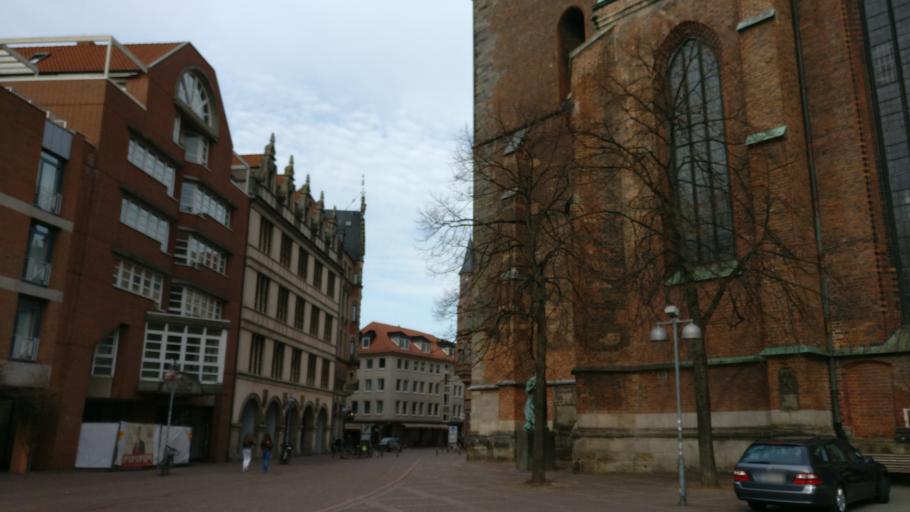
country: DE
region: Lower Saxony
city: Hannover
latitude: 52.3716
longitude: 9.7353
